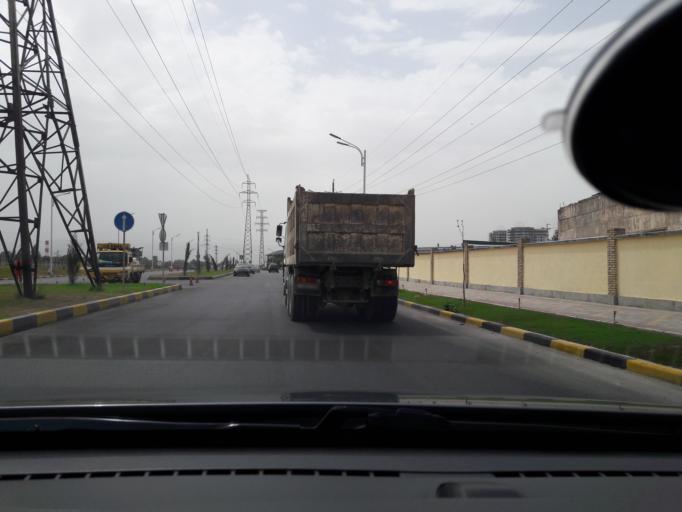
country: TJ
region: Dushanbe
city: Dushanbe
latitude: 38.5656
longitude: 68.7682
